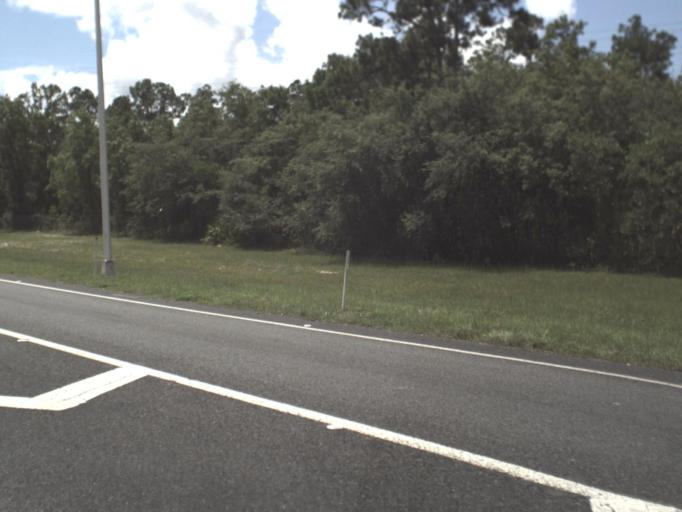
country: US
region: Florida
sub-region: Flagler County
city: Palm Coast
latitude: 29.6604
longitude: -81.2842
